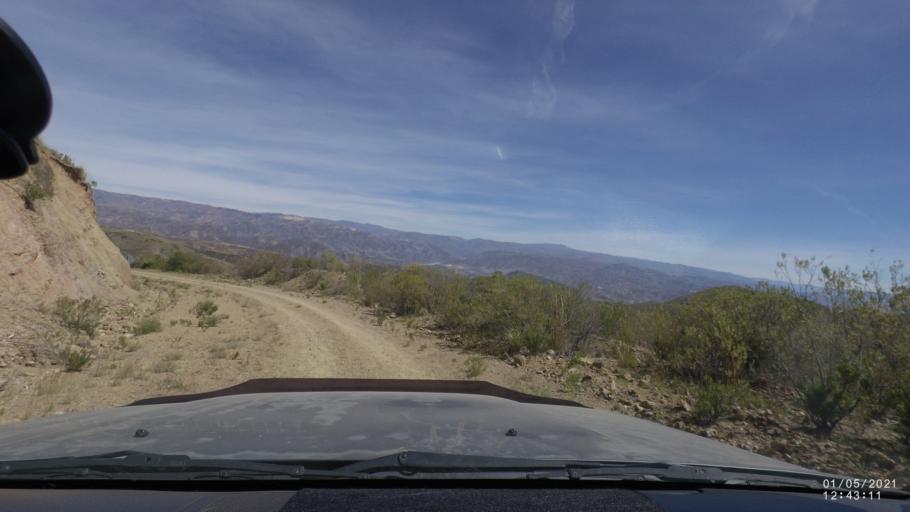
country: BO
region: Cochabamba
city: Capinota
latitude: -17.6792
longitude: -66.1602
